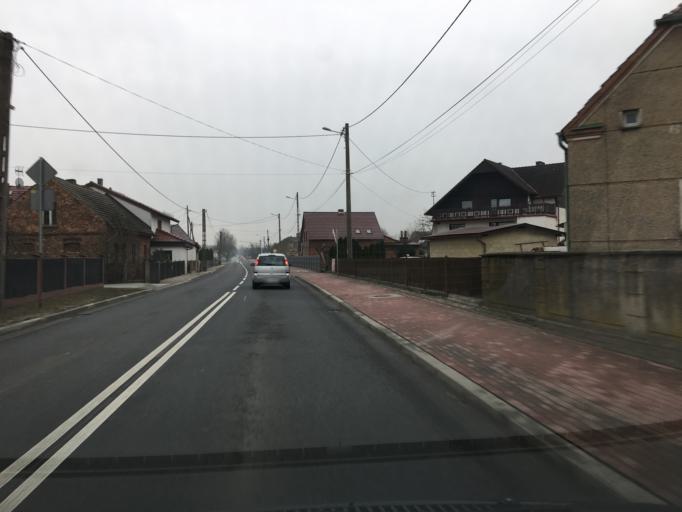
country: PL
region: Opole Voivodeship
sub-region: Powiat kedzierzynsko-kozielski
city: Kedzierzyn-Kozle
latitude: 50.3146
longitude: 18.2252
